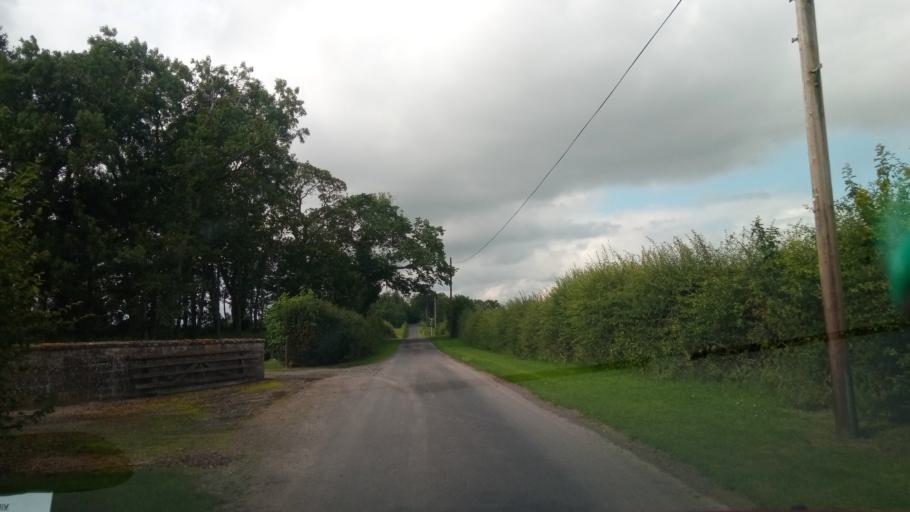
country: GB
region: Scotland
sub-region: The Scottish Borders
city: Hawick
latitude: 55.4414
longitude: -2.7026
